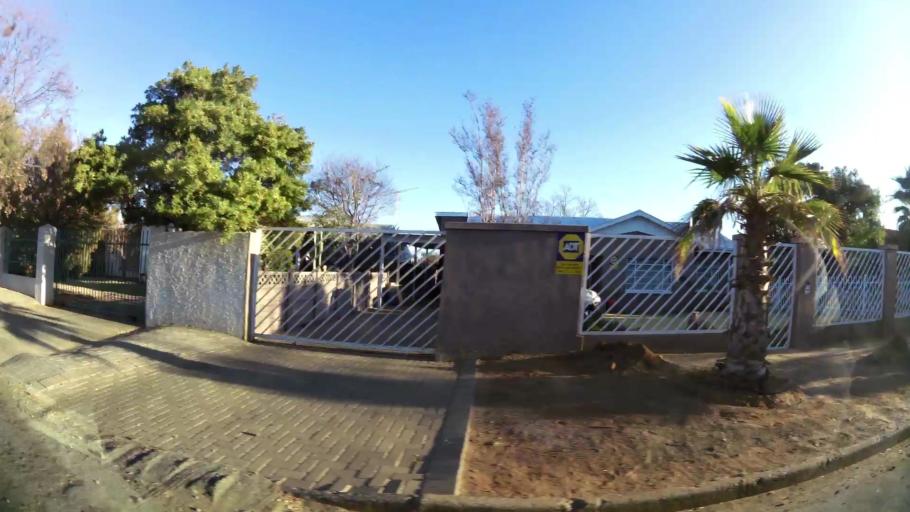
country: ZA
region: Northern Cape
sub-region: Frances Baard District Municipality
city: Kimberley
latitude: -28.7537
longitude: 24.7389
